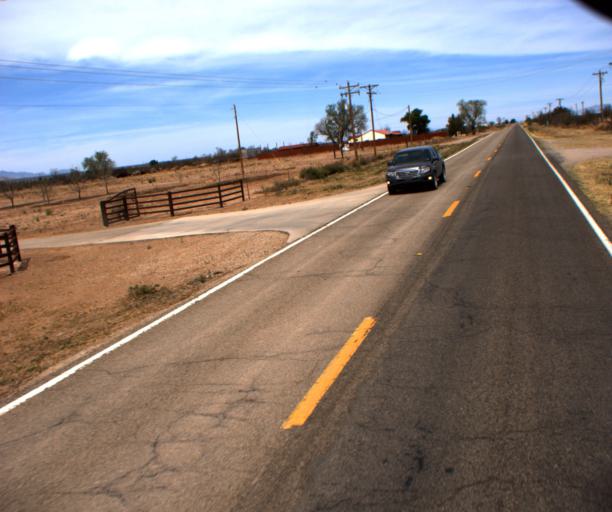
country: US
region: Arizona
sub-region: Cochise County
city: Bisbee
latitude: 31.7065
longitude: -109.6872
